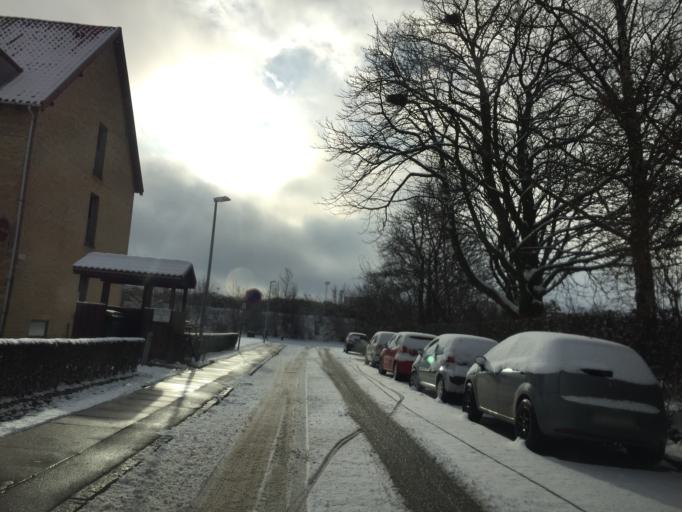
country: DK
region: Capital Region
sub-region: Tarnby Kommune
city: Tarnby
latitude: 55.6315
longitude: 12.6416
